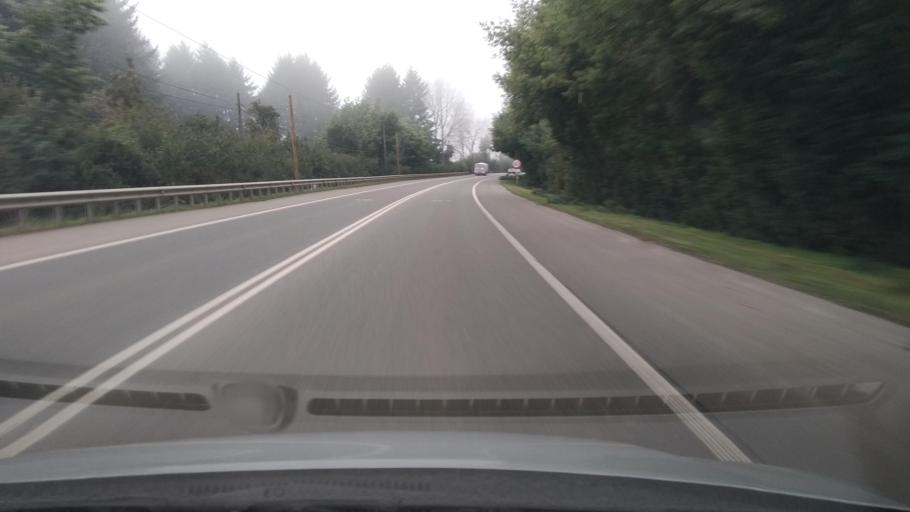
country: CL
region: Los Lagos
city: Las Animas
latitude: -39.7364
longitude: -73.2220
